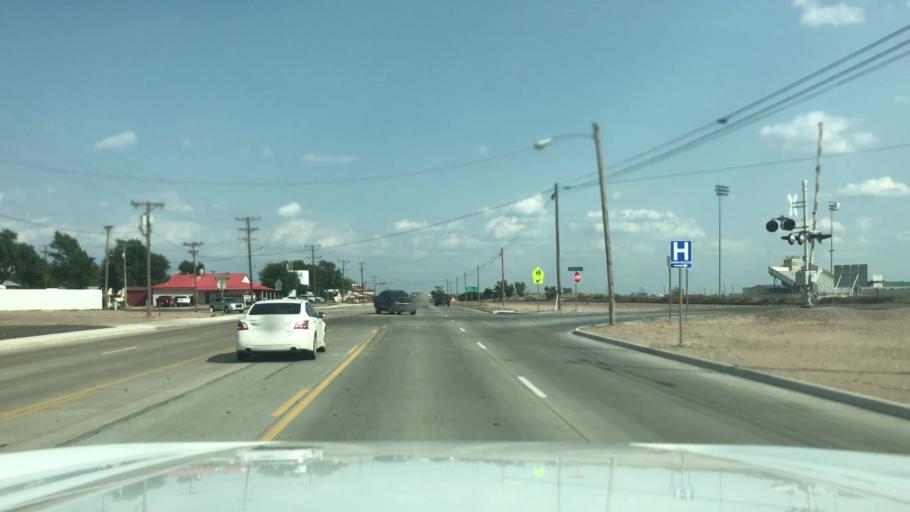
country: US
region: Texas
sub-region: Dallam County
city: Dalhart
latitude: 36.0513
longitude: -102.5012
